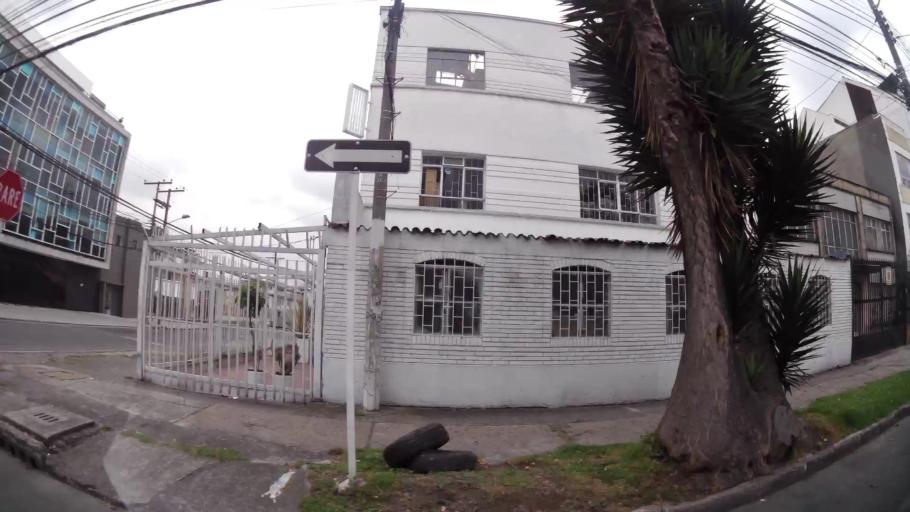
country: CO
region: Bogota D.C.
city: Barrio San Luis
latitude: 4.6647
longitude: -74.0638
